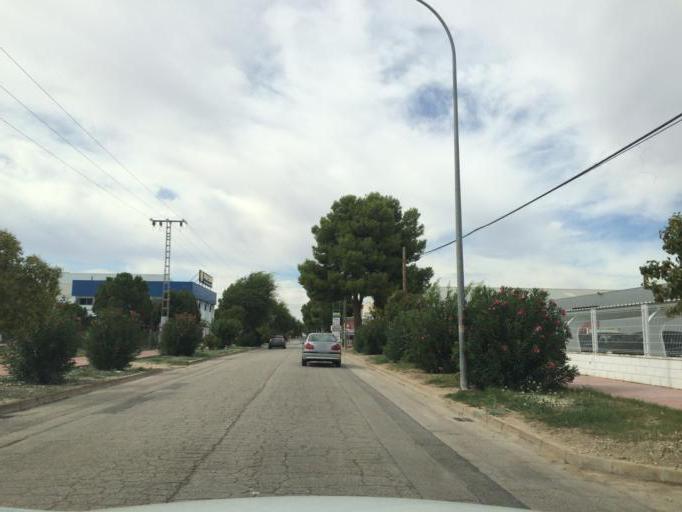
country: ES
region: Castille-La Mancha
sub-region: Provincia de Albacete
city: Albacete
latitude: 39.0151
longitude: -1.8824
